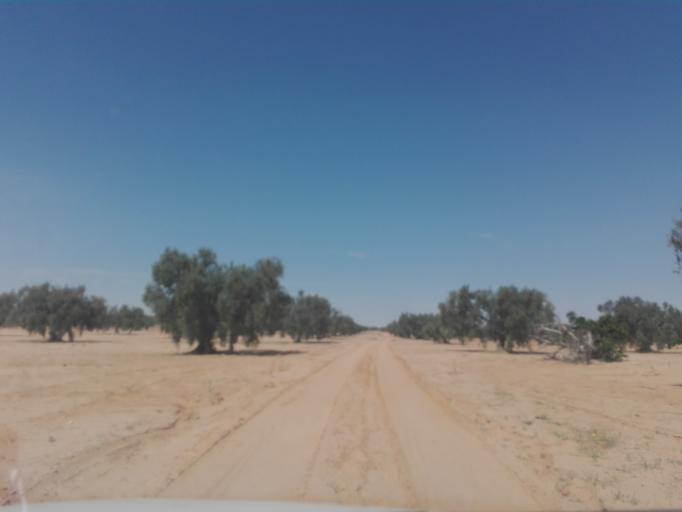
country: TN
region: Safaqis
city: Bi'r `Ali Bin Khalifah
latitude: 34.6623
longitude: 10.3151
